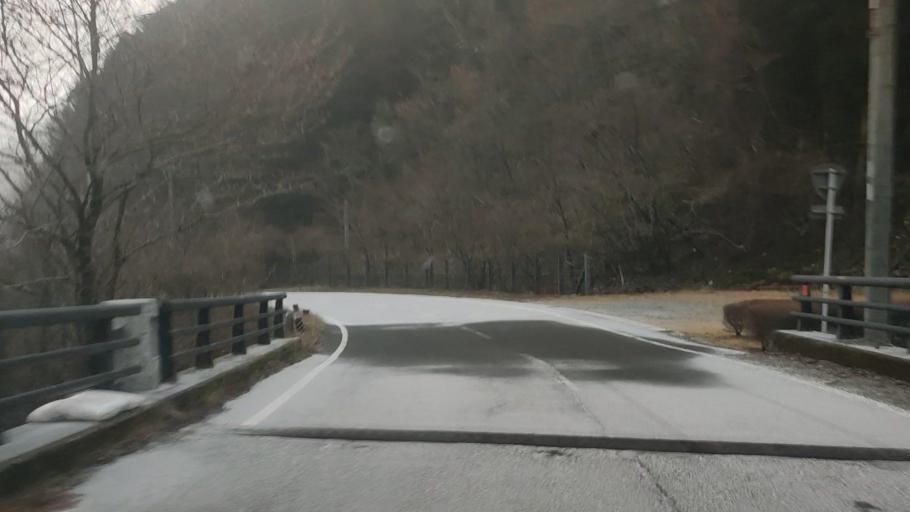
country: JP
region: Kumamoto
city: Matsubase
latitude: 32.5599
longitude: 130.9173
